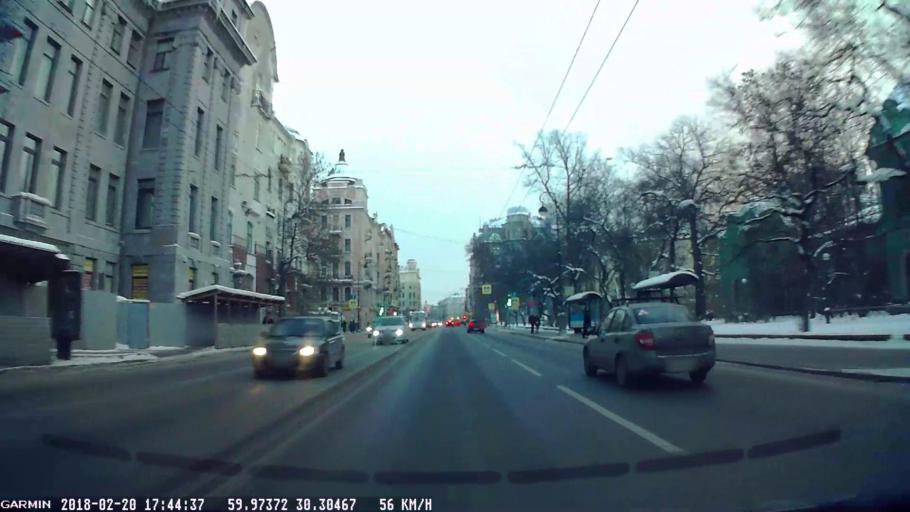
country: RU
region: St.-Petersburg
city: Petrogradka
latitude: 59.9732
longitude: 30.3051
